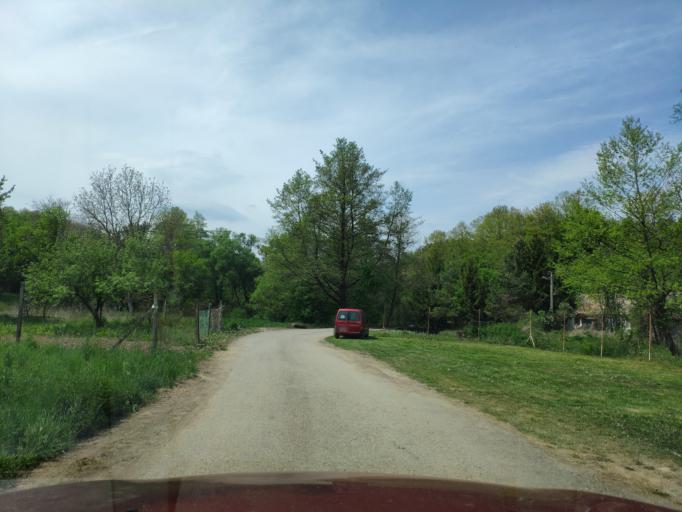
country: SK
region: Banskobystricky
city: Rimavska Sobota
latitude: 48.4842
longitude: 20.0700
